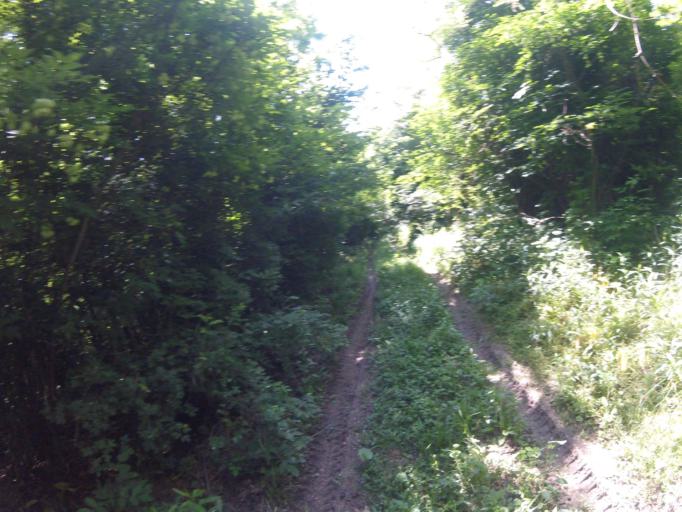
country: HU
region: Zala
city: Zalaszentgrot
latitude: 46.9117
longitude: 17.0417
